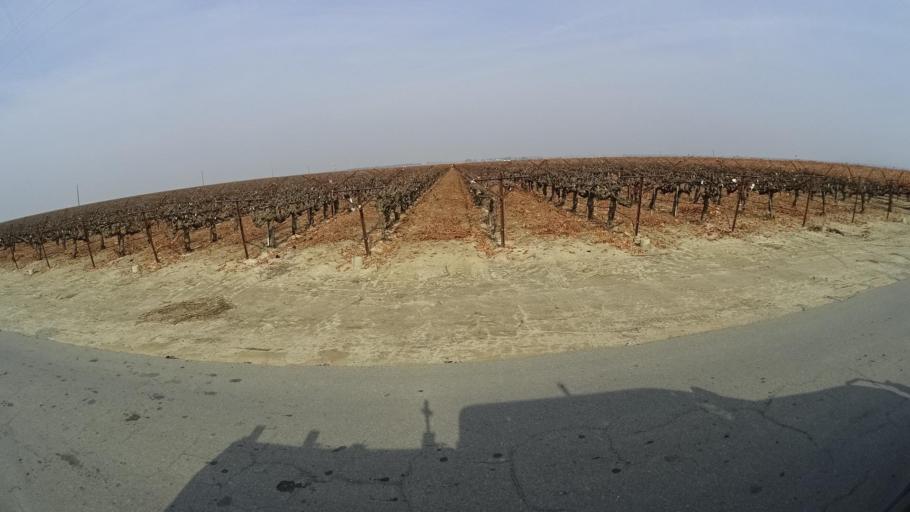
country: US
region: California
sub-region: Kern County
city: Arvin
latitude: 35.0745
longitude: -118.9204
